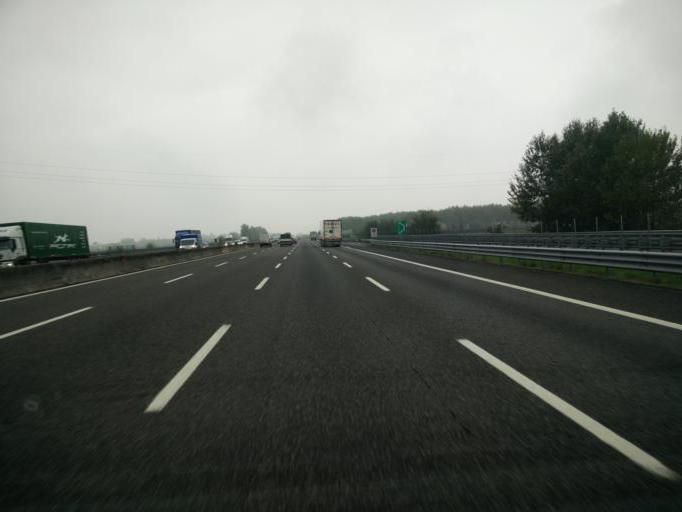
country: IT
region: Emilia-Romagna
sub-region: Provincia di Modena
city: Montale
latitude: 44.6100
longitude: 10.9050
